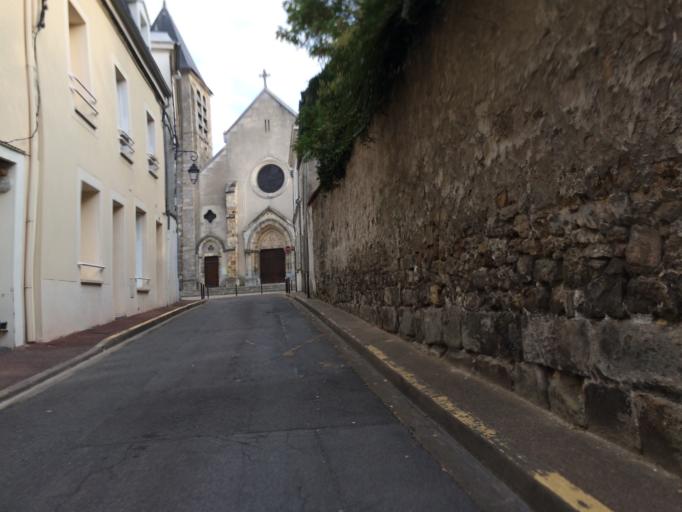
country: FR
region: Ile-de-France
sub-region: Departement de l'Essonne
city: Montlhery
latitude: 48.6381
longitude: 2.2711
